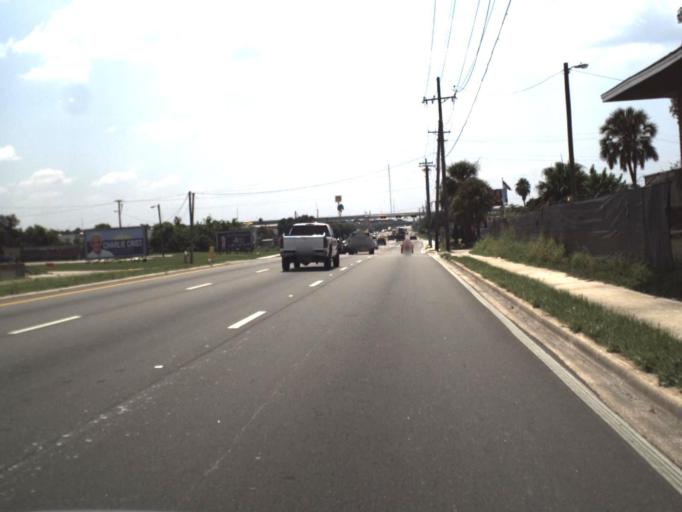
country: US
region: Florida
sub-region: Hillsborough County
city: East Lake-Orient Park
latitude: 27.9581
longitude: -82.4019
